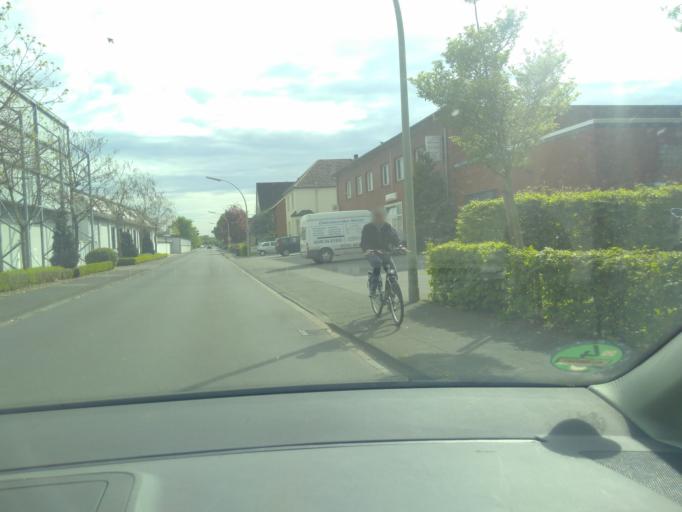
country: DE
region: North Rhine-Westphalia
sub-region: Regierungsbezirk Detmold
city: Rheda-Wiedenbruck
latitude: 51.8288
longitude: 8.3085
